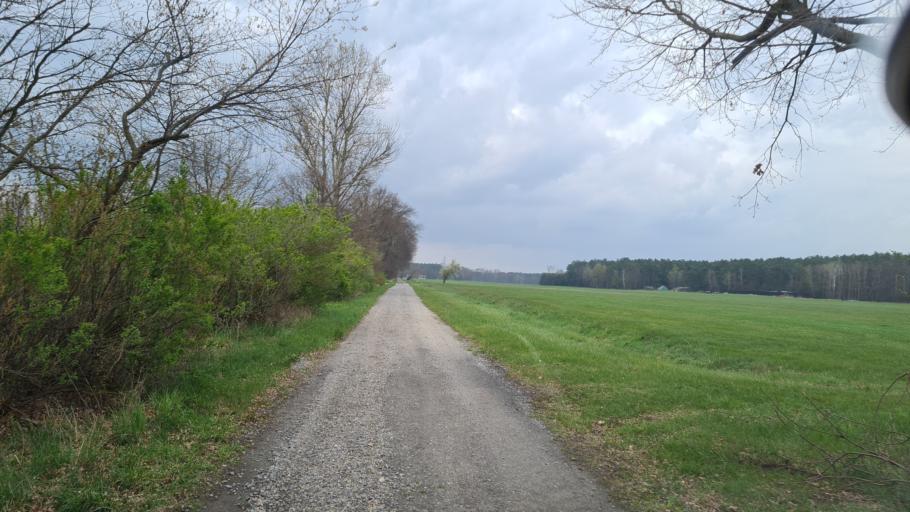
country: DE
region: Brandenburg
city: Sallgast
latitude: 51.6165
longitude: 13.8689
